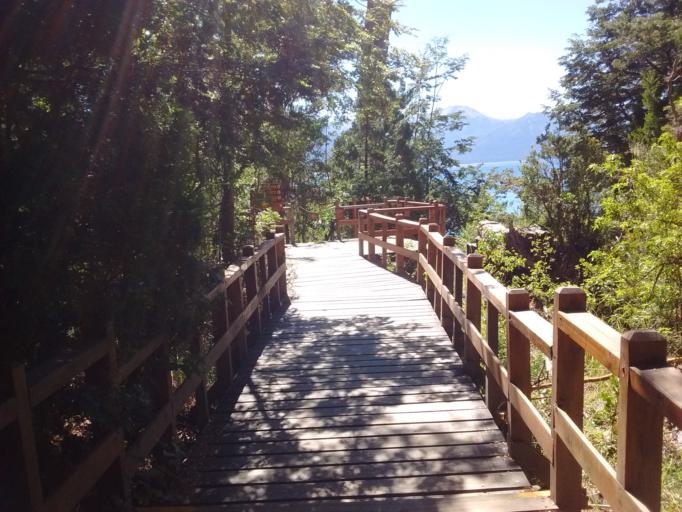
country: AR
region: Neuquen
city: Villa La Angostura
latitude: -40.8570
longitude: -71.6139
